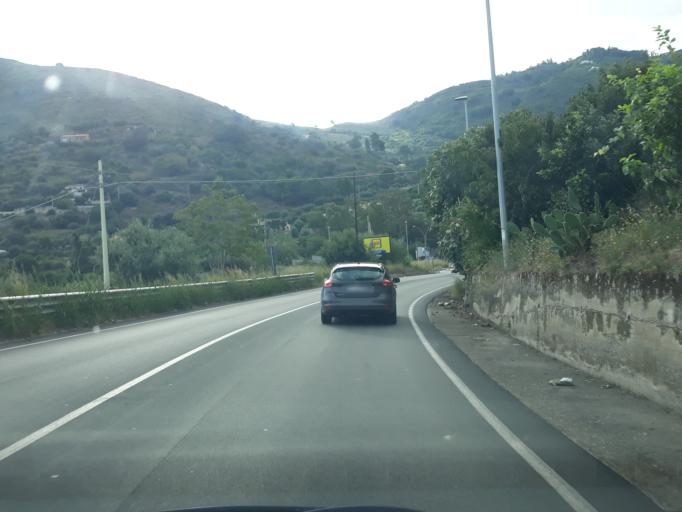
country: IT
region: Sicily
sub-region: Palermo
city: Cefalu
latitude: 38.0273
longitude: 14.0130
